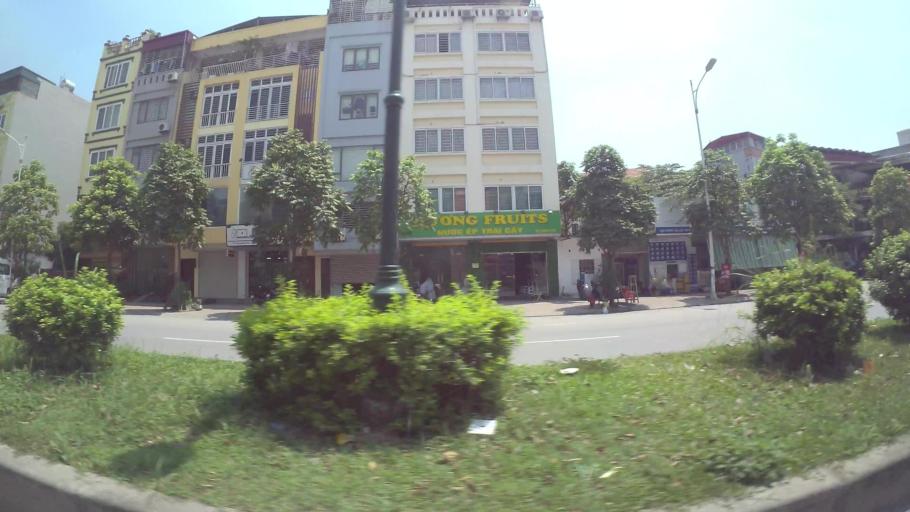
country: VN
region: Ha Noi
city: Hoan Kiem
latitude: 21.0414
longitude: 105.8747
